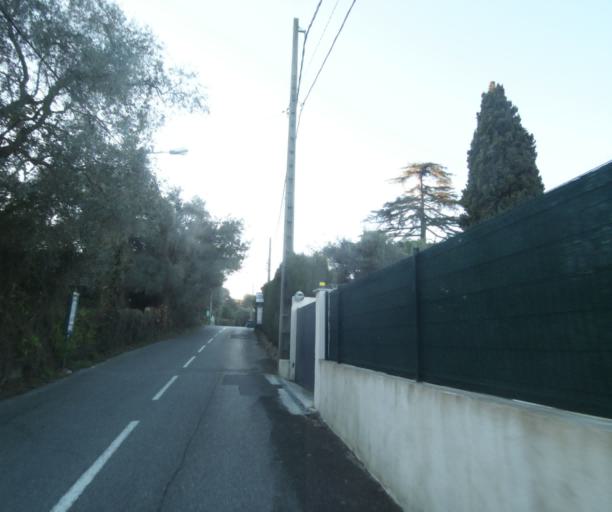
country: FR
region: Provence-Alpes-Cote d'Azur
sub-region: Departement des Alpes-Maritimes
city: Vallauris
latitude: 43.5860
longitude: 7.0809
